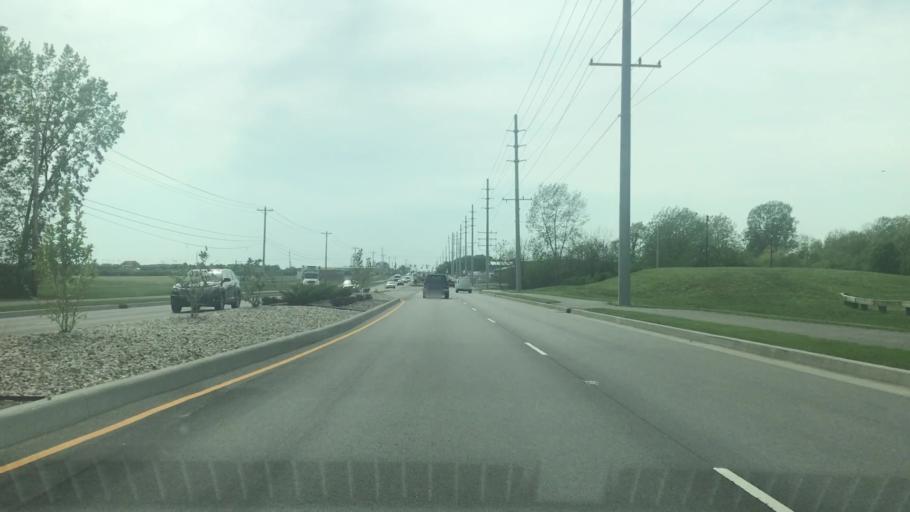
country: US
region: Indiana
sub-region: Johnson County
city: New Whiteland
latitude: 39.5868
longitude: -86.0934
